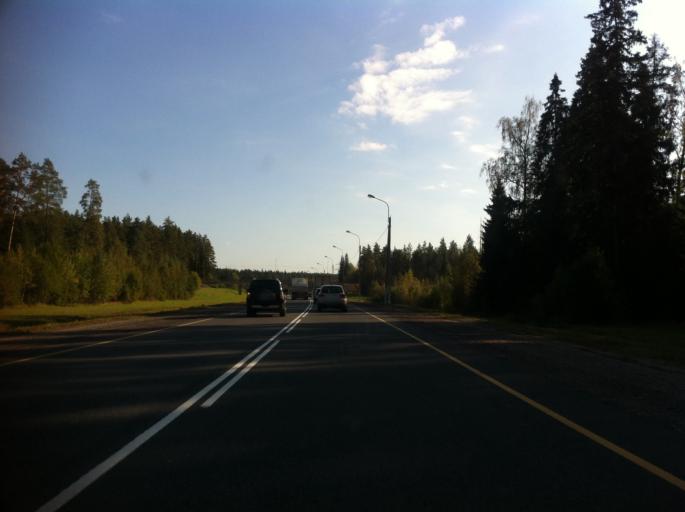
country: RU
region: Leningrad
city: Luga
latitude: 58.7604
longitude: 29.8849
